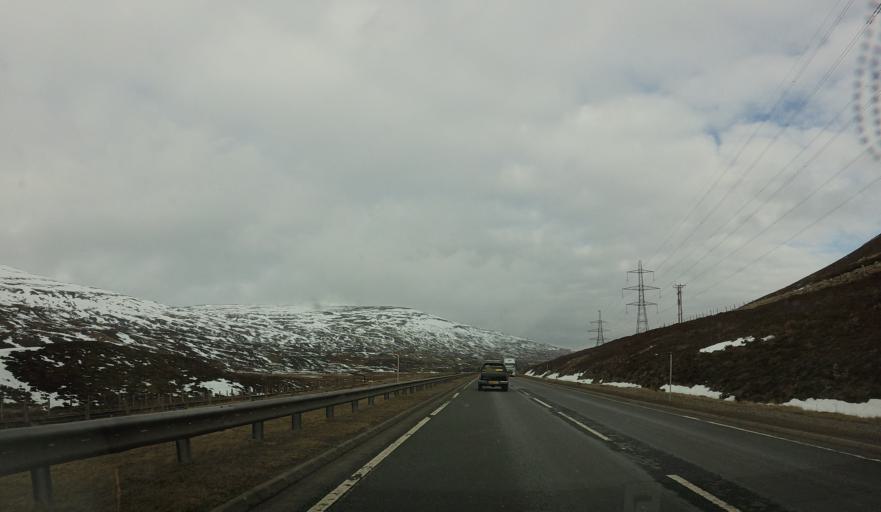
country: GB
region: Scotland
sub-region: Highland
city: Kingussie
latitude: 56.8708
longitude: -4.2567
